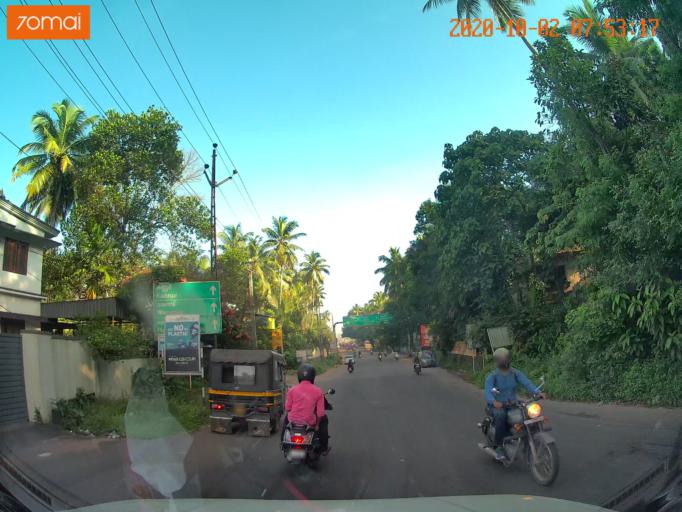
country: IN
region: Kerala
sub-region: Kozhikode
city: Ferokh
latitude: 11.1663
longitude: 75.8760
